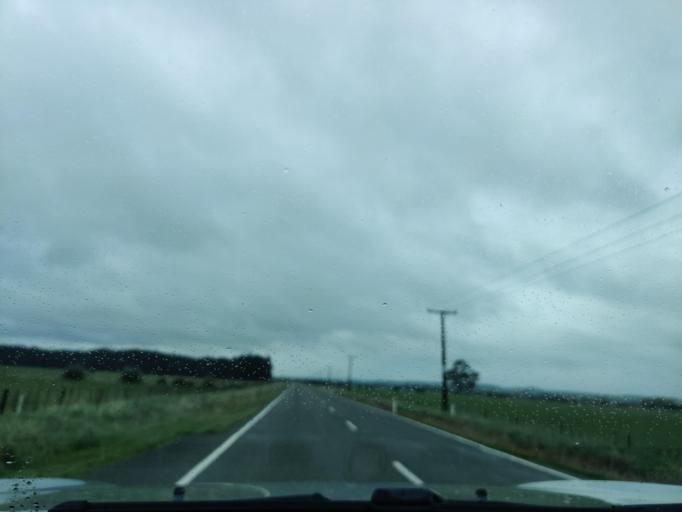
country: NZ
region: Hawke's Bay
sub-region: Hastings District
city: Hastings
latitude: -40.0098
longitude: 176.3781
